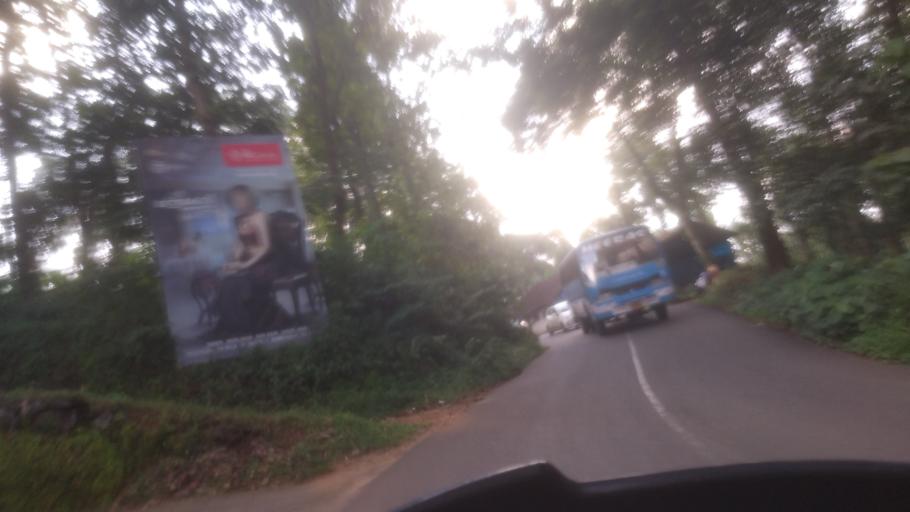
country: IN
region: Kerala
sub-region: Ernakulam
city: Kotamangalam
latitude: 10.0062
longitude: 76.6761
